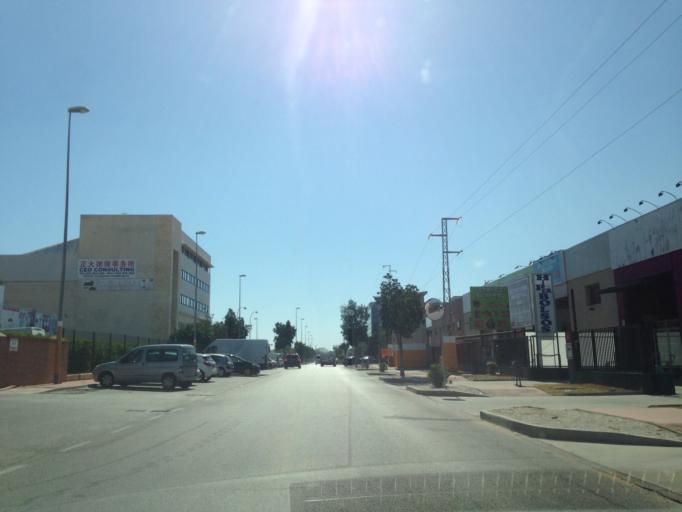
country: ES
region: Andalusia
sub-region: Provincia de Malaga
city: Malaga
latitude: 36.6910
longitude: -4.4727
